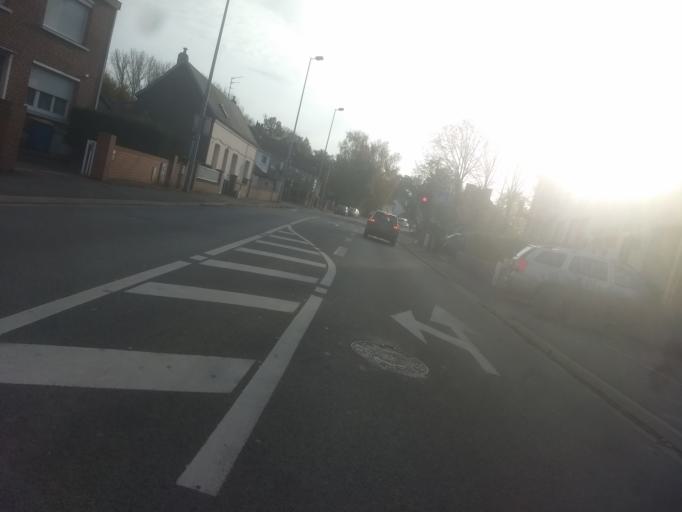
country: FR
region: Nord-Pas-de-Calais
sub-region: Departement du Pas-de-Calais
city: Achicourt
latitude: 50.2677
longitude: 2.7539
